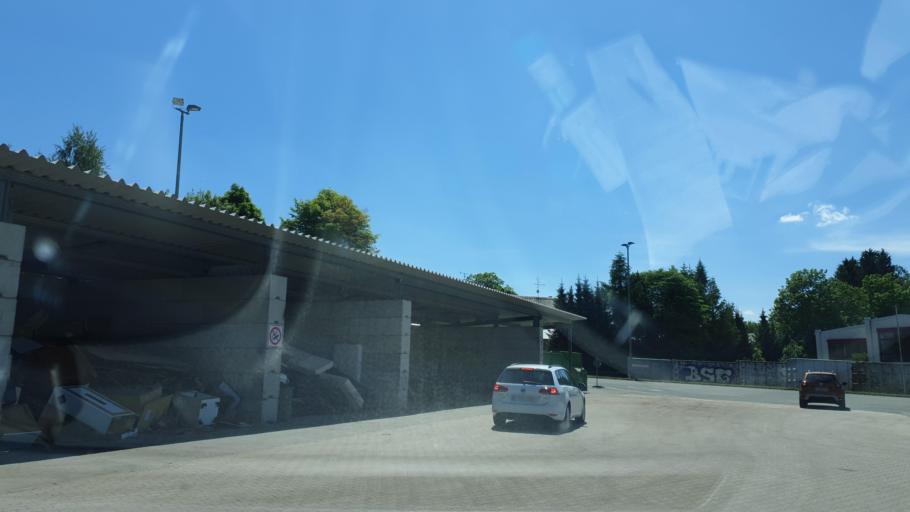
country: DE
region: Saxony
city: Neustadt Vogtland
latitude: 50.4751
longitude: 12.3487
